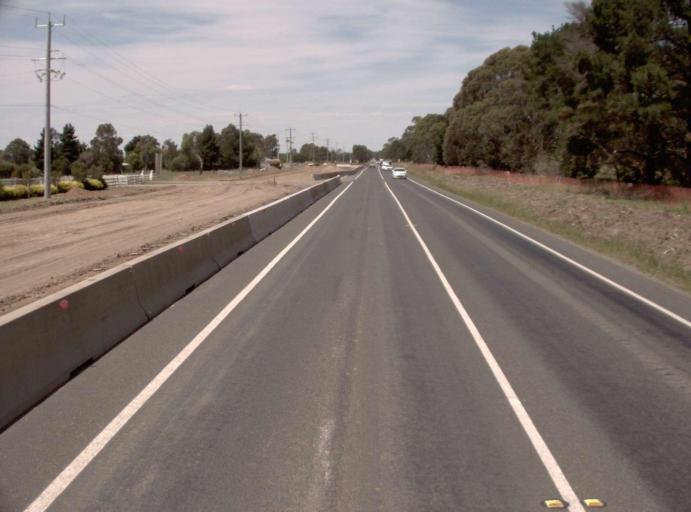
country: AU
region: Victoria
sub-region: Latrobe
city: Traralgon
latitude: -38.1863
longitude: 146.5874
